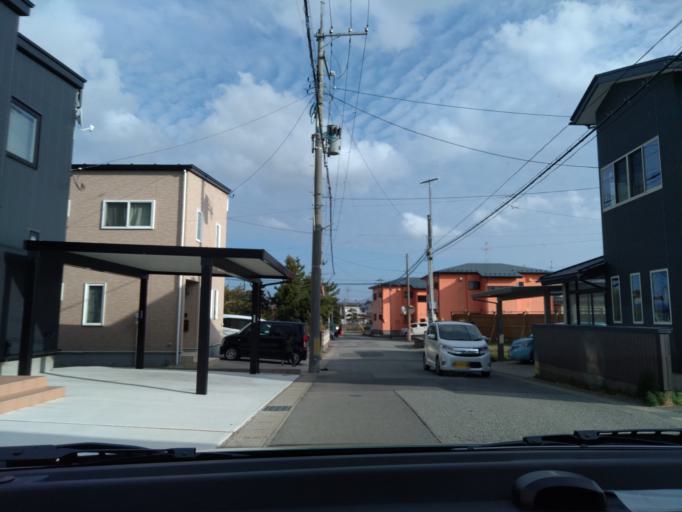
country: JP
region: Akita
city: Akita Shi
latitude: 39.7700
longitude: 140.0825
